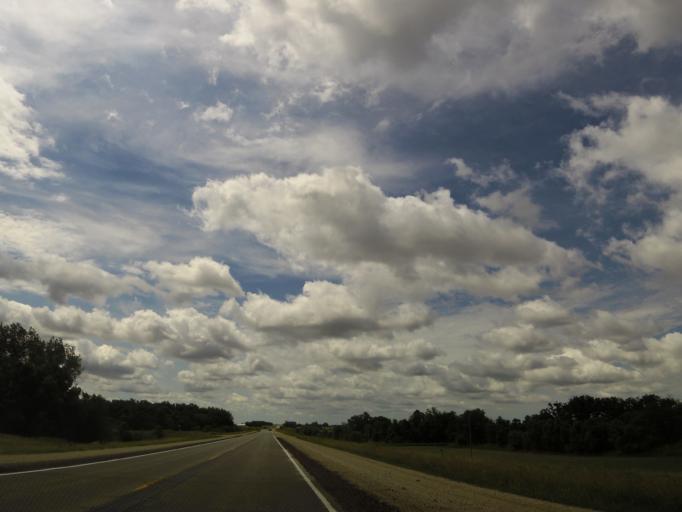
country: US
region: Iowa
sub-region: Chickasaw County
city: New Hampton
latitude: 43.2433
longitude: -92.2992
